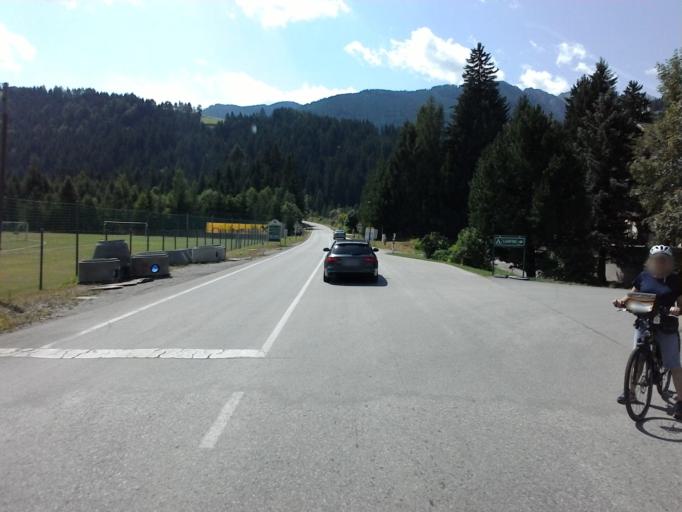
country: AT
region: Tyrol
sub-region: Politischer Bezirk Lienz
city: Heinfels
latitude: 46.7468
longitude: 12.4662
